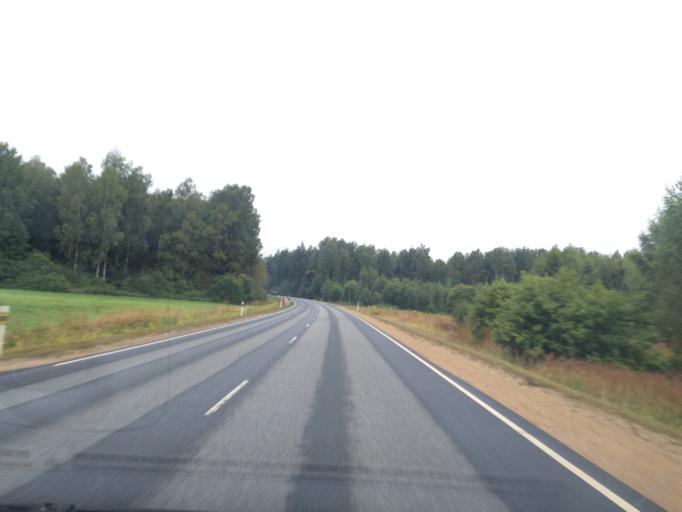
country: LV
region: Ogre
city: Ogre
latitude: 56.8581
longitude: 24.5902
